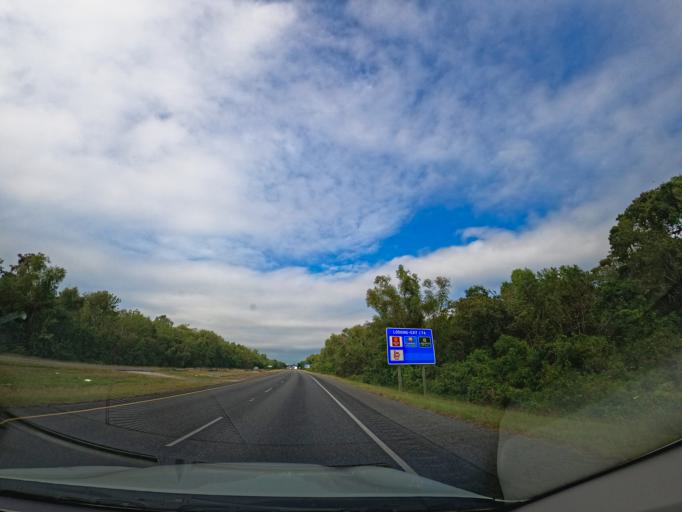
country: US
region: Louisiana
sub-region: Saint Mary Parish
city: Morgan City
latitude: 29.6973
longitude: -91.1639
